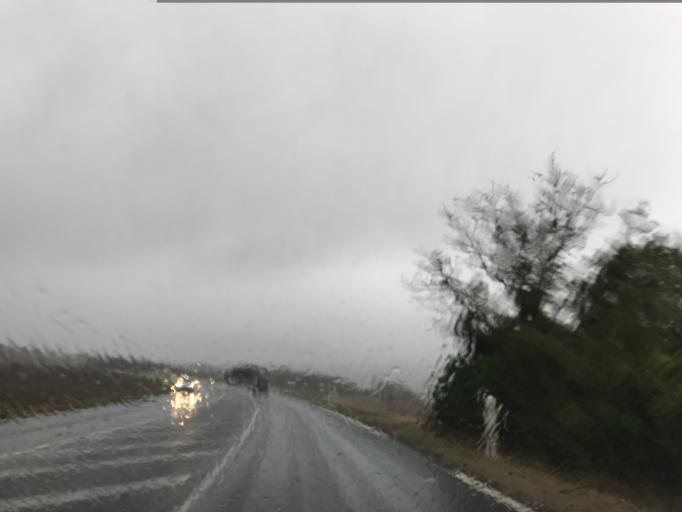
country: FR
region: Auvergne
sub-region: Departement du Puy-de-Dome
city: Dallet
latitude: 45.7729
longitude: 3.2223
